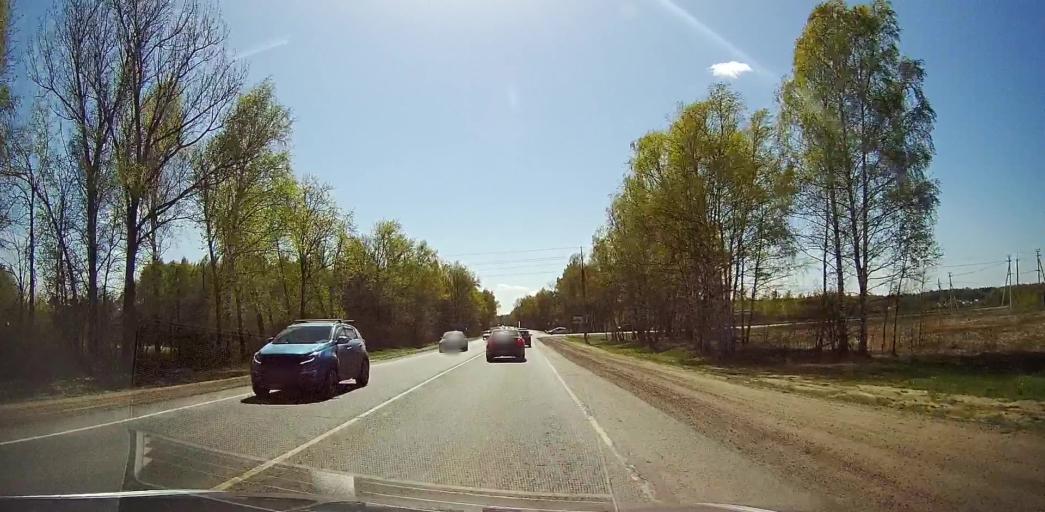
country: RU
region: Moskovskaya
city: Malyshevo
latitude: 55.4535
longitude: 38.3265
